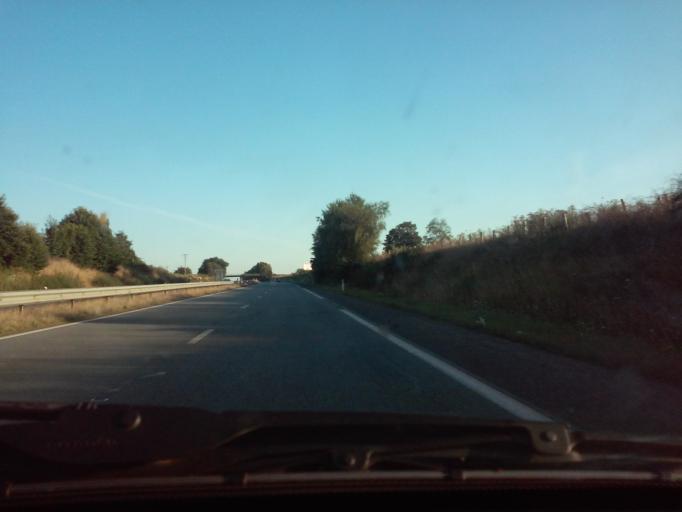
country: FR
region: Brittany
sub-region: Departement des Cotes-d'Armor
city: Saint-Samson-sur-Rance
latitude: 48.5124
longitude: -2.0393
